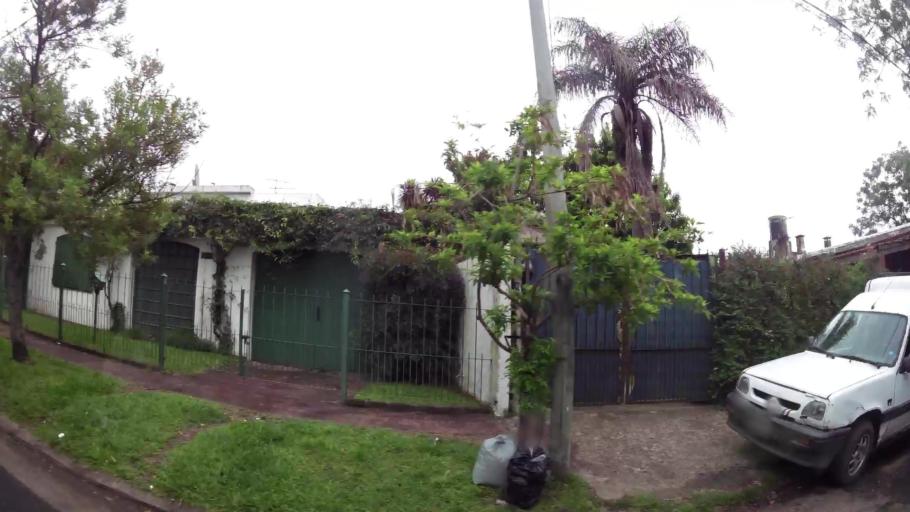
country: AR
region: Buenos Aires
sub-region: Partido de Quilmes
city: Quilmes
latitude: -34.7615
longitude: -58.1997
